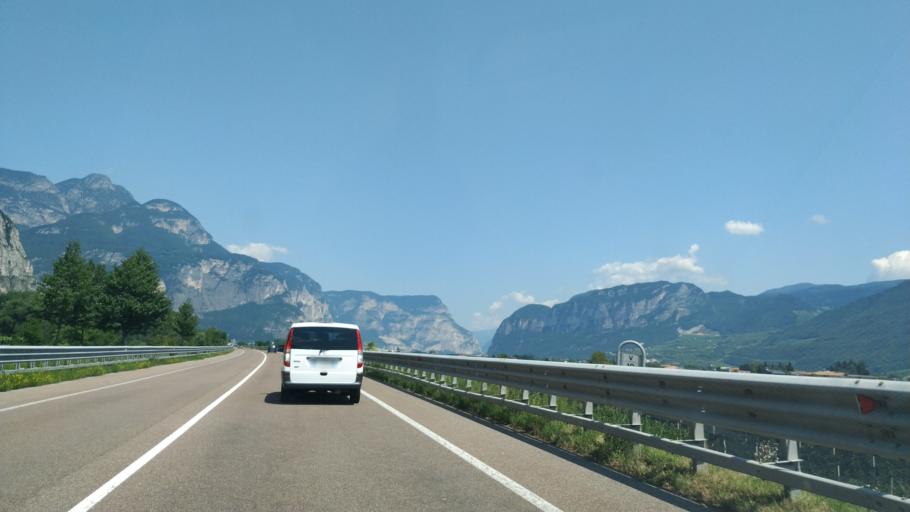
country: IT
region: Trentino-Alto Adige
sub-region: Provincia di Trento
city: Nave San Rocco
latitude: 46.1739
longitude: 11.0906
